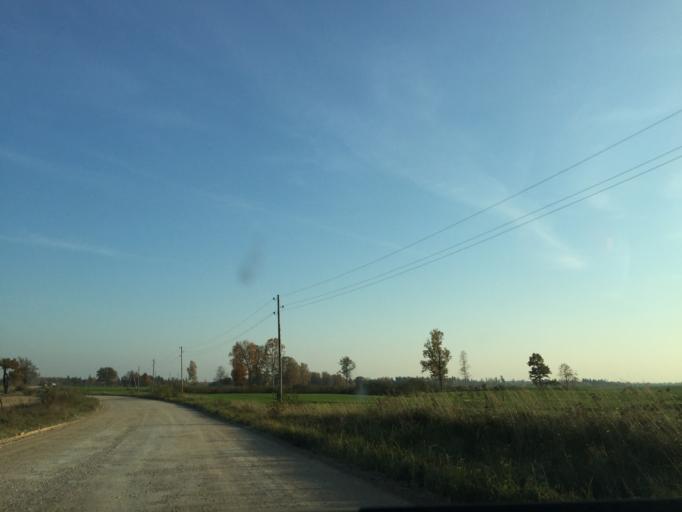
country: LV
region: Vainode
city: Vainode
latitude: 56.6121
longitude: 21.8174
